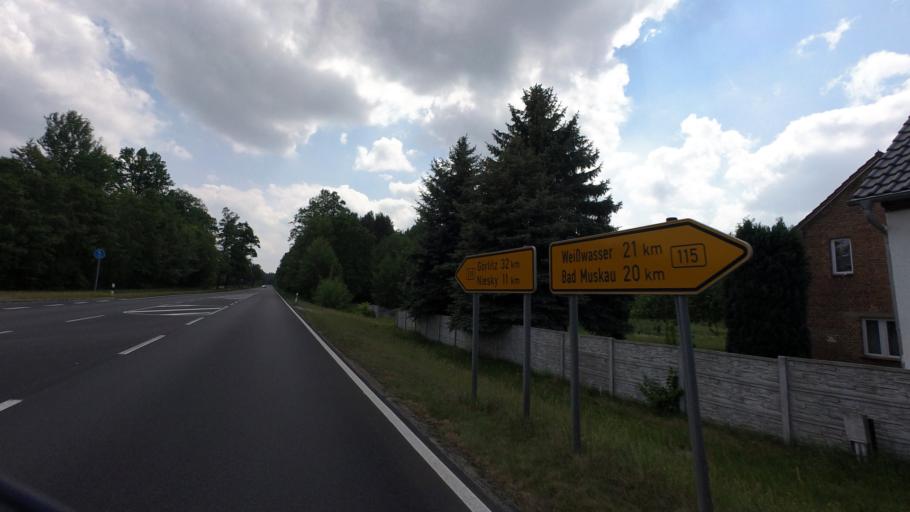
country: DE
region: Saxony
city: Rietschen
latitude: 51.3828
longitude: 14.7877
